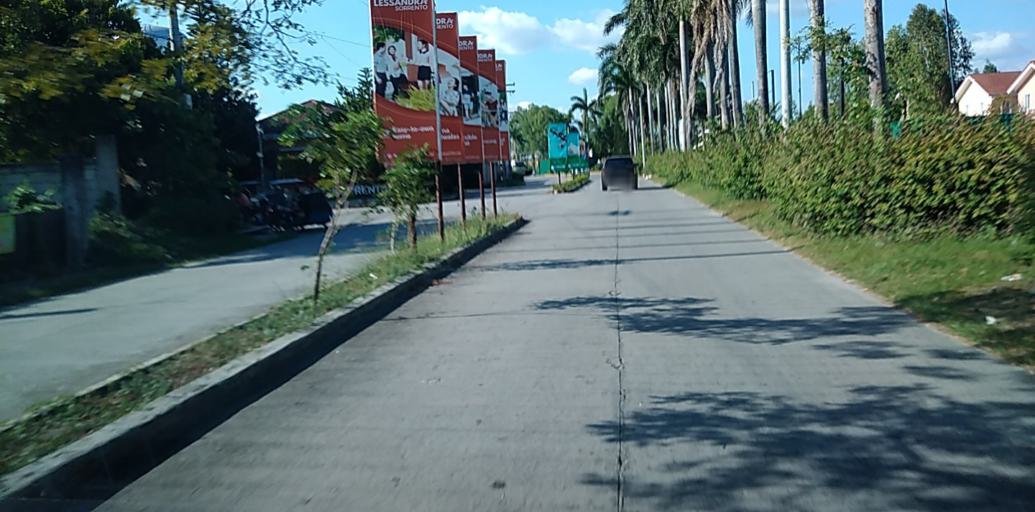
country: PH
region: Central Luzon
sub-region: Province of Pampanga
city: Acli
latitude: 15.1085
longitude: 120.6538
